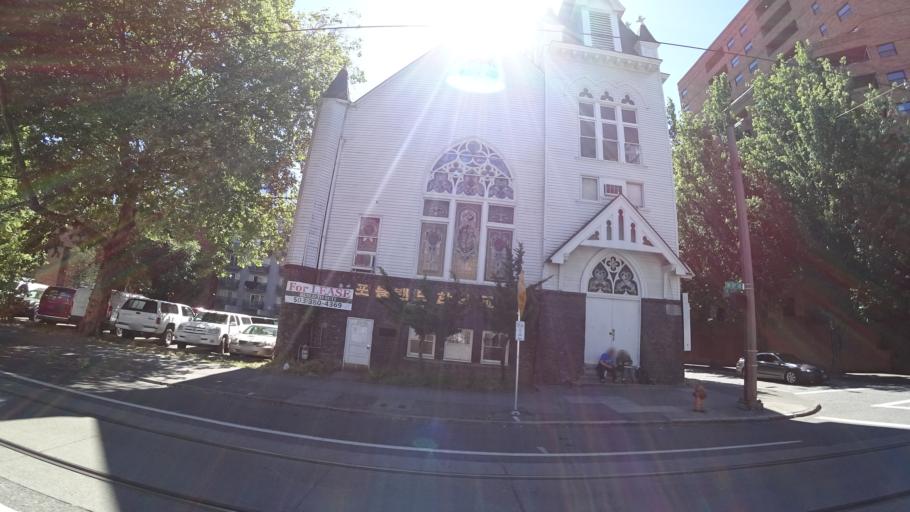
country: US
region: Oregon
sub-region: Multnomah County
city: Portland
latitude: 45.5148
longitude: -122.6850
